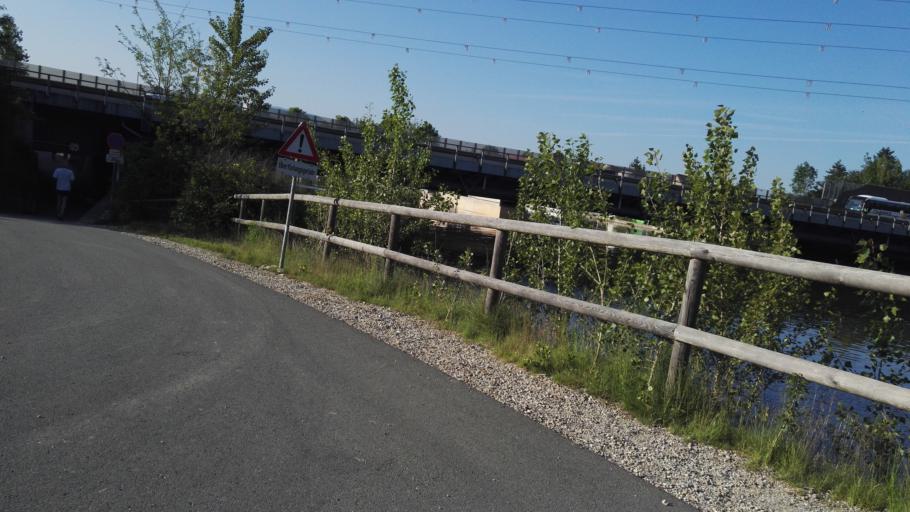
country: AT
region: Styria
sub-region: Politischer Bezirk Graz-Umgebung
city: Feldkirchen bei Graz
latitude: 47.0141
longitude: 15.4591
